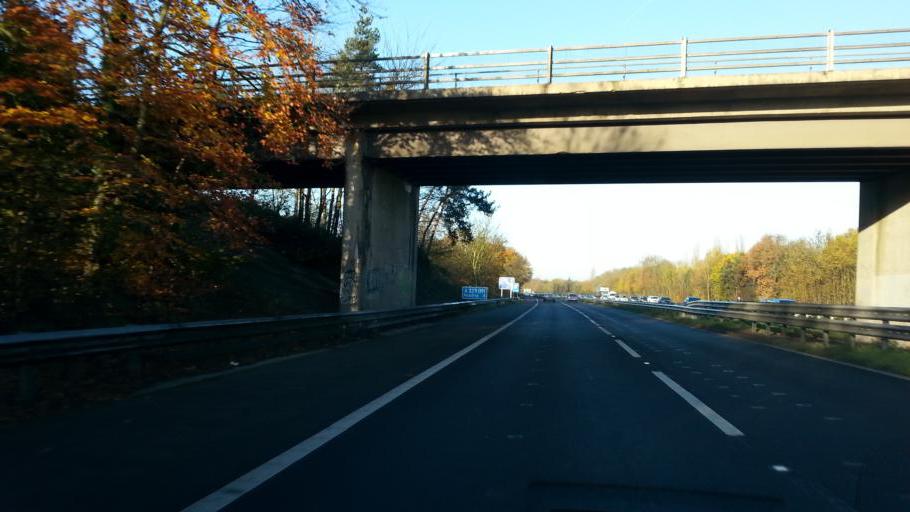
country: GB
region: England
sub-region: Wokingham
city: Winnersh
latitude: 51.4377
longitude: -0.8720
